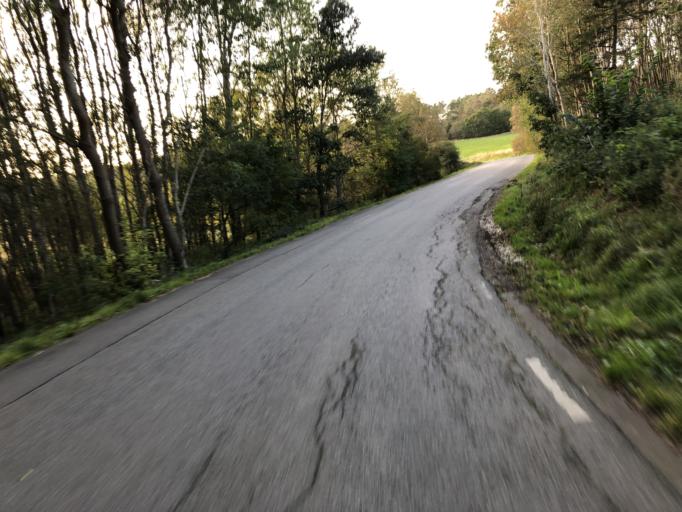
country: SE
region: Vaestra Goetaland
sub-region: Goteborg
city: Torslanda
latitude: 57.7347
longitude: 11.8419
